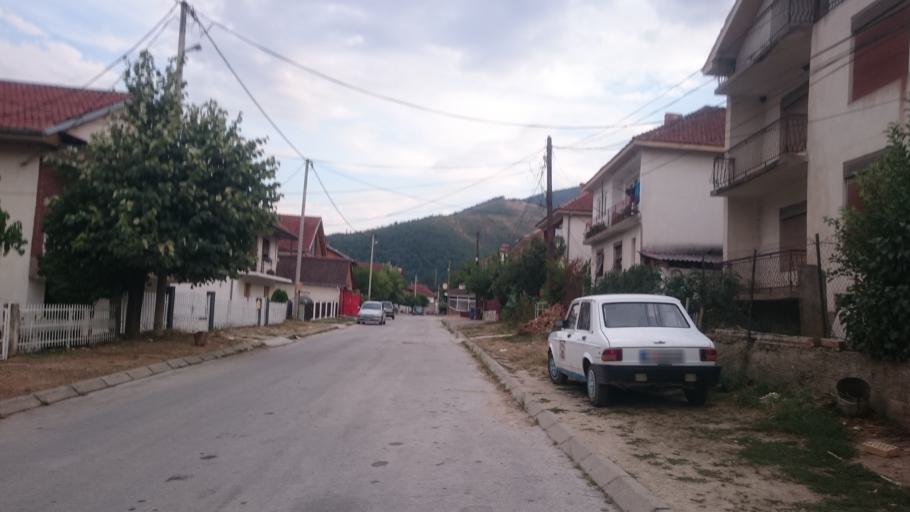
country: MK
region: Makedonski Brod
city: Makedonski Brod
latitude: 41.5133
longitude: 21.2145
